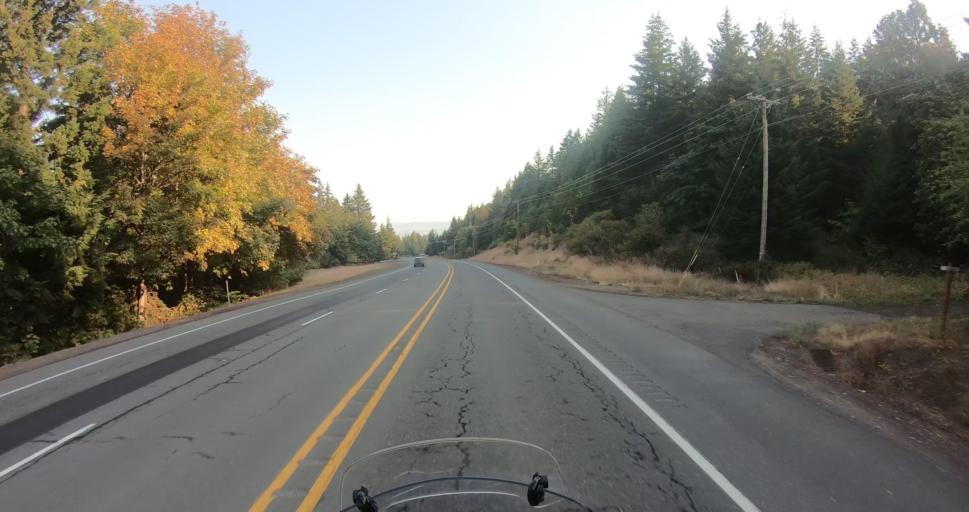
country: US
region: Oregon
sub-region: Hood River County
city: Odell
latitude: 45.5967
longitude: -121.5493
